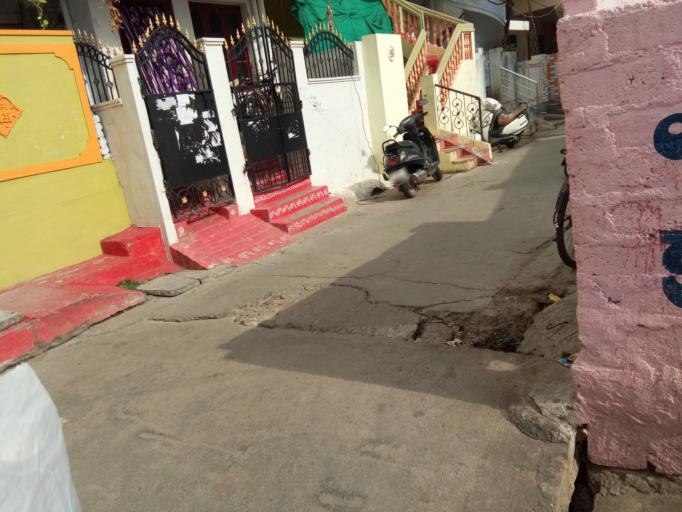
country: IN
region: Telangana
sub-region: Khammam
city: Khammam
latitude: 17.2419
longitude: 80.1427
